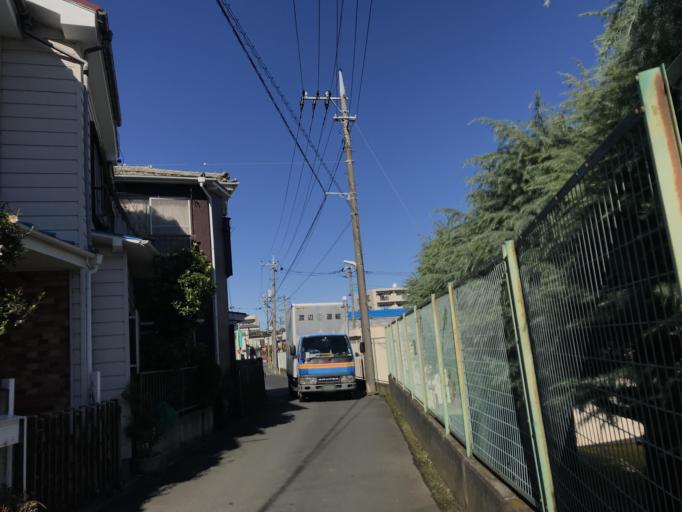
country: JP
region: Tokyo
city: Tanashicho
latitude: 35.7573
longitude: 139.5123
